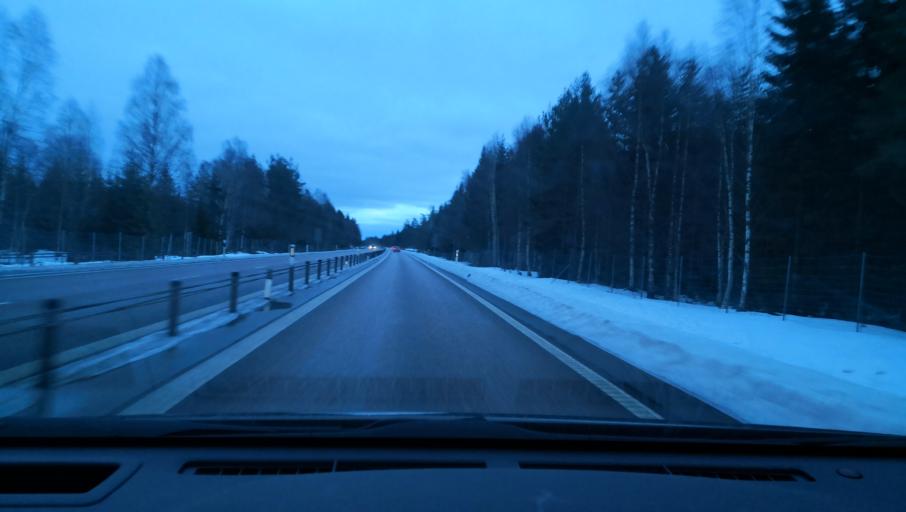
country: SE
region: Vaestmanland
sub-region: Surahammars Kommun
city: Ramnas
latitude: 59.8284
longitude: 16.0879
